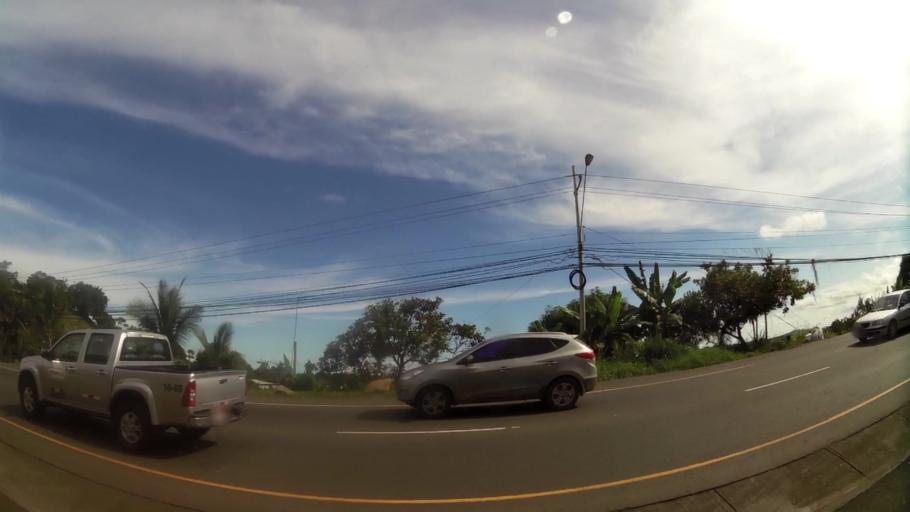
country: PA
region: Panama
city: La Chorrera
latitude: 8.8896
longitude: -79.7650
